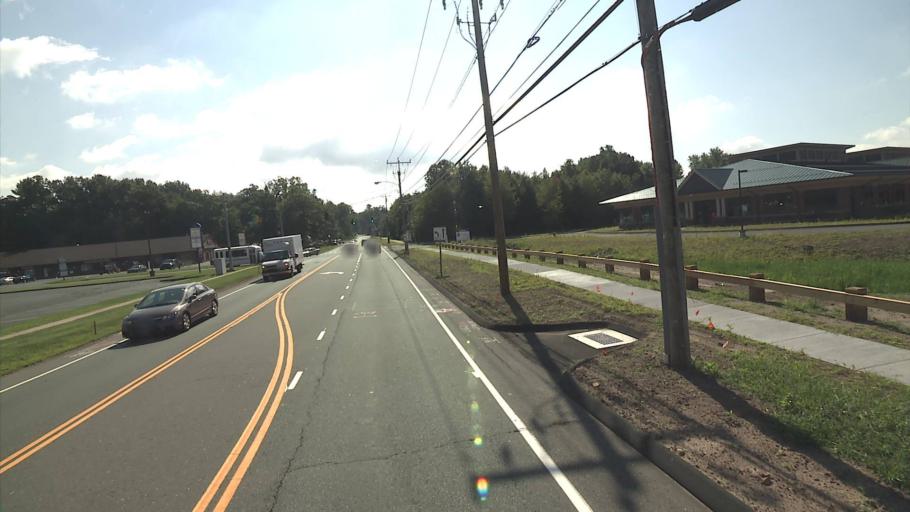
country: US
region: Connecticut
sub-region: Hartford County
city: Hazardville
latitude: 41.9876
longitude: -72.5579
